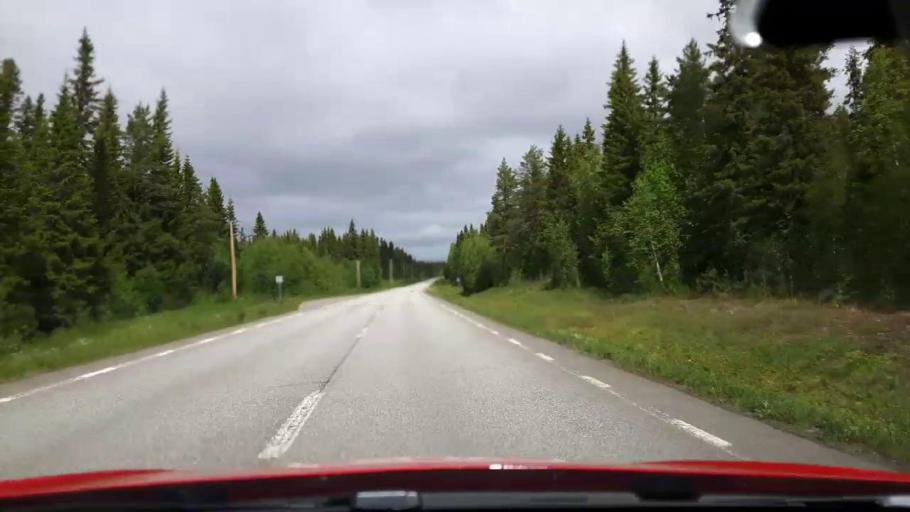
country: SE
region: Jaemtland
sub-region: Krokoms Kommun
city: Krokom
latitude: 63.4855
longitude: 14.5051
